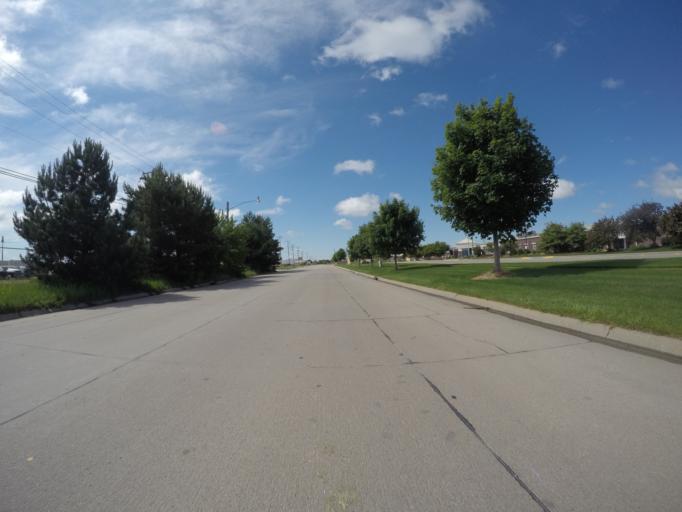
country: US
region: Nebraska
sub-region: Buffalo County
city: Kearney
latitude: 40.6835
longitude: -99.0876
